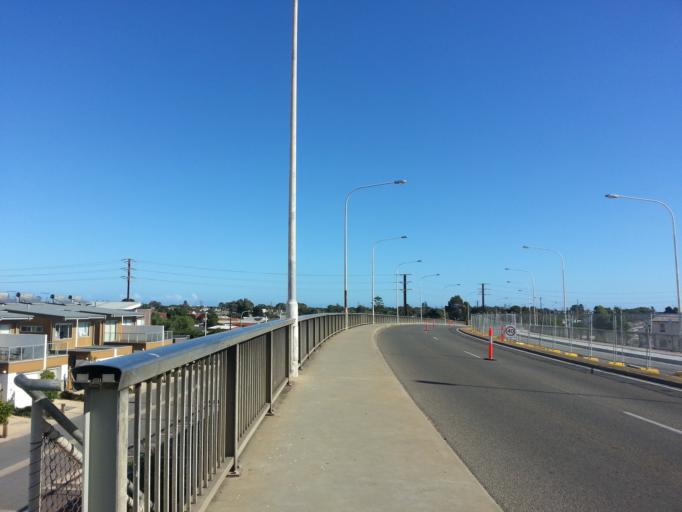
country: AU
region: South Australia
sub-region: Port Adelaide Enfield
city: Birkenhead
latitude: -34.8467
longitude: 138.4957
